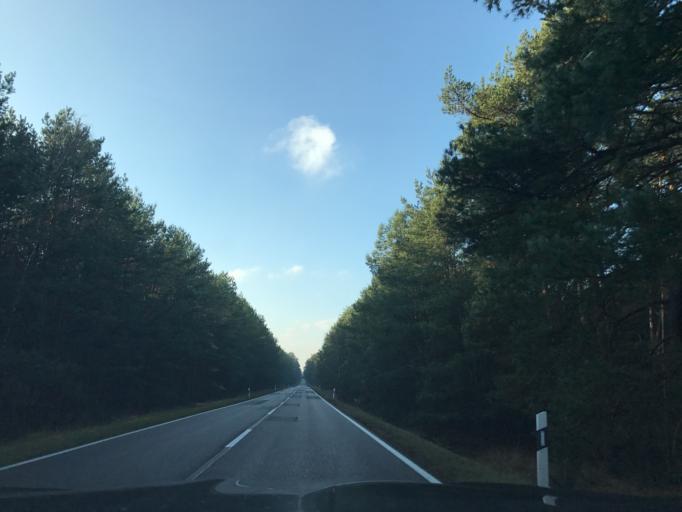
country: DE
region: Brandenburg
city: Wenzlow
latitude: 52.2779
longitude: 12.4289
